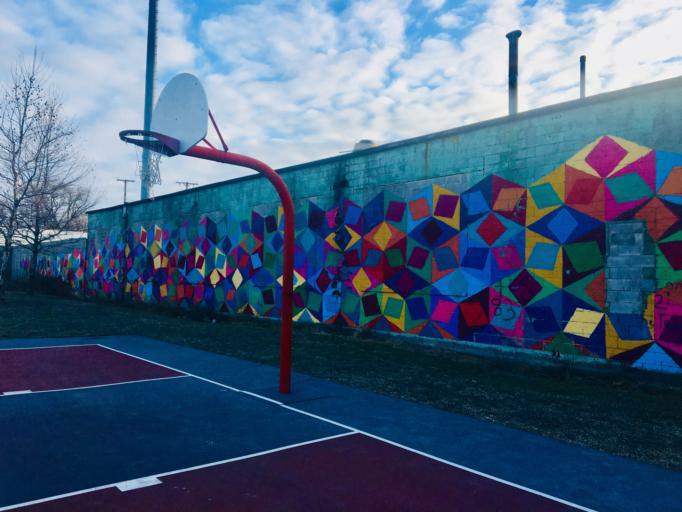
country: US
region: Michigan
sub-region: Oakland County
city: Oak Park
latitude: 42.3950
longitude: -83.1818
